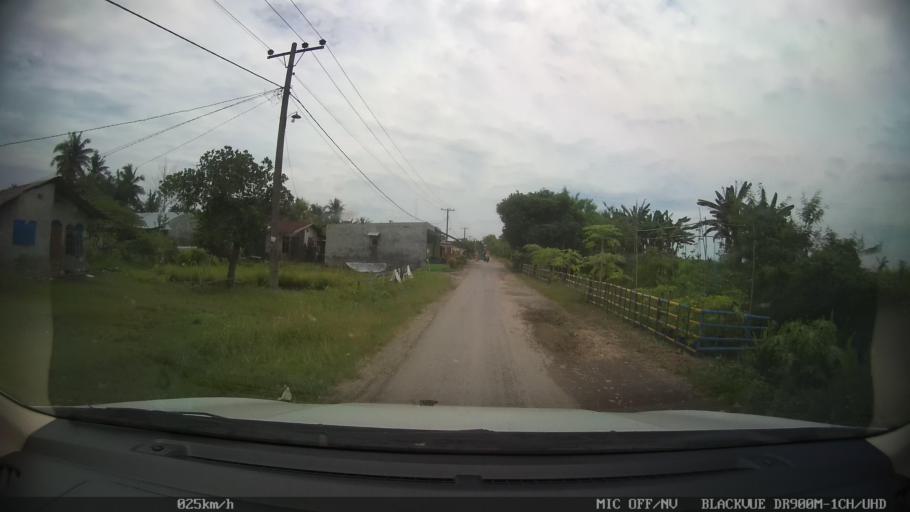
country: ID
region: North Sumatra
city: Sunggal
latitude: 3.6350
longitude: 98.5729
